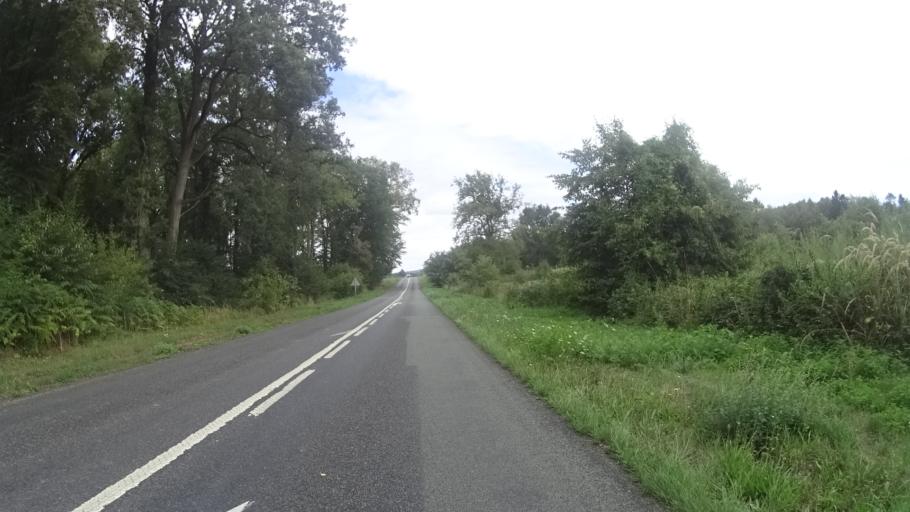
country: FR
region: Picardie
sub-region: Departement de l'Oise
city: Noyon
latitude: 49.5502
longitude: 2.9875
